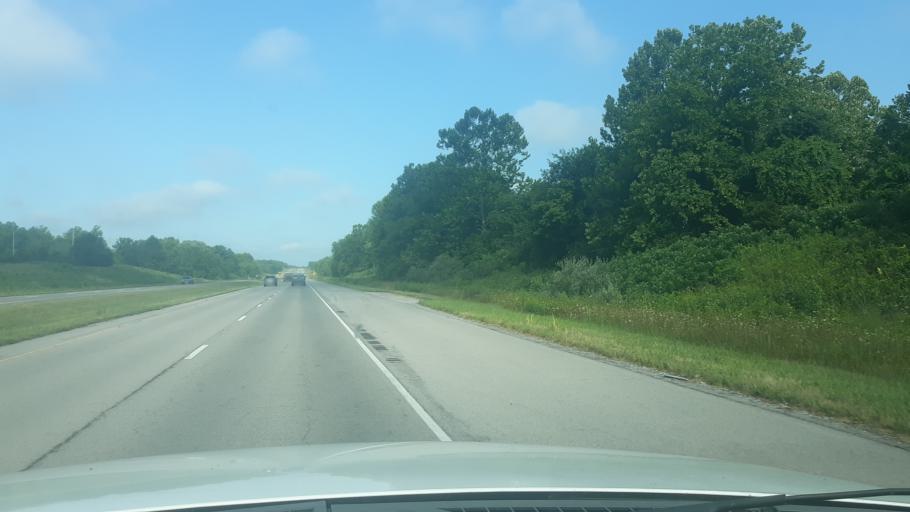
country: US
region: Illinois
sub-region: Saline County
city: Carrier Mills
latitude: 37.7308
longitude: -88.7452
